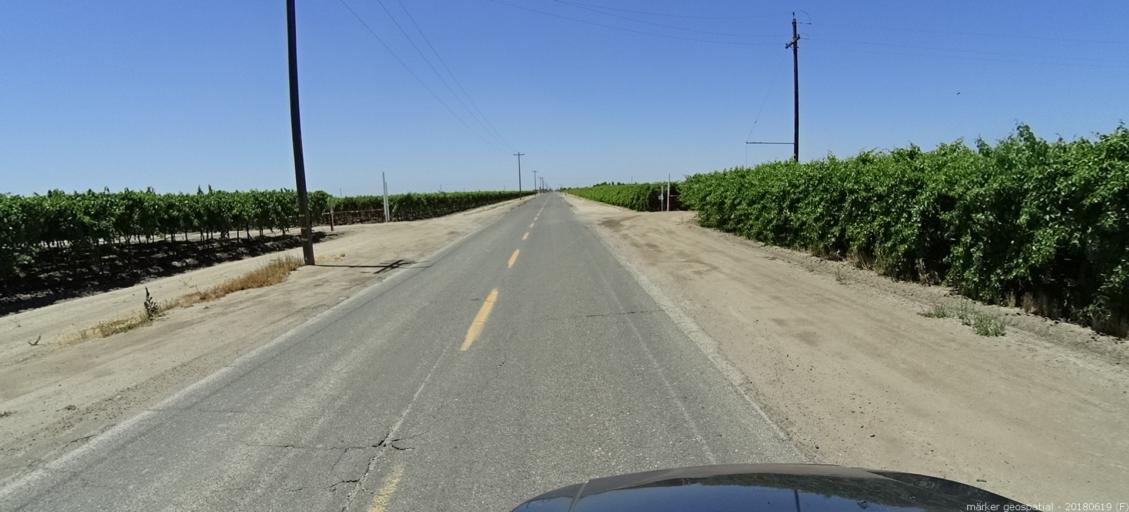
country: US
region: California
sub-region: Madera County
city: Parkwood
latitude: 36.8658
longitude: -120.0871
